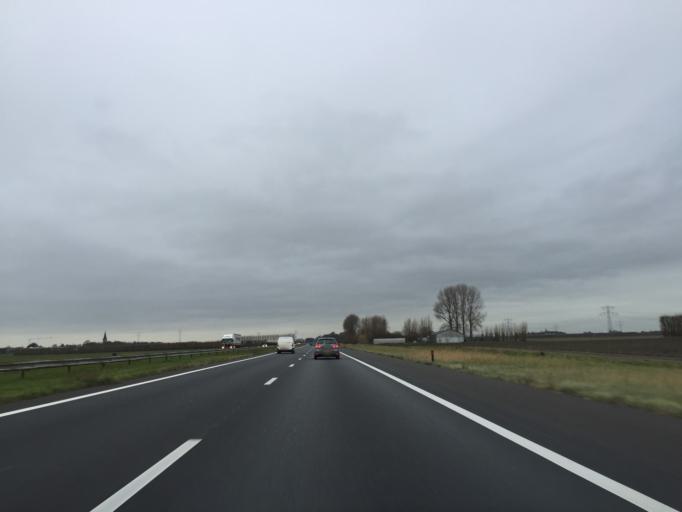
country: NL
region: Zeeland
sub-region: Gemeente Reimerswaal
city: Yerseke
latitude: 51.4441
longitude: 4.0553
